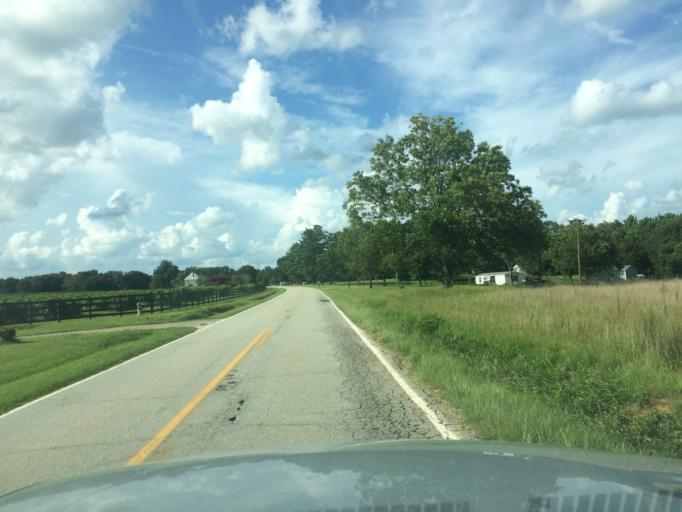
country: US
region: South Carolina
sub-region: Spartanburg County
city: Woodruff
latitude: 34.7728
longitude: -82.1116
